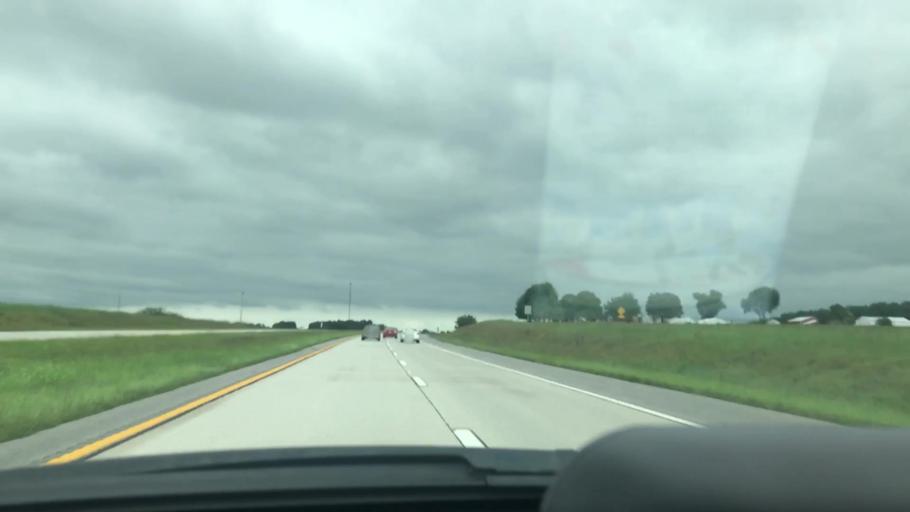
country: US
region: Missouri
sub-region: Greene County
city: Fair Grove
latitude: 37.4431
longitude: -93.1442
